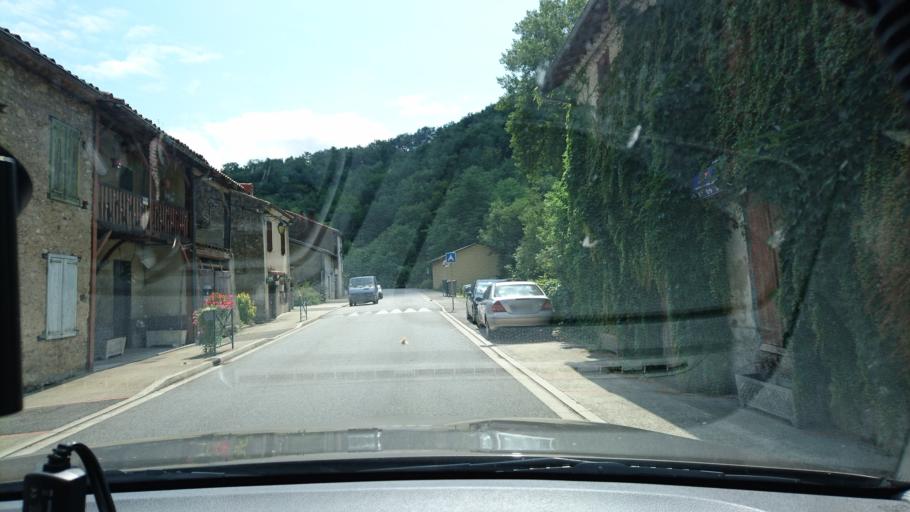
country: FR
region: Midi-Pyrenees
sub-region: Departement de la Haute-Garonne
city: Gaillac-Toulza
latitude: 43.1010
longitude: 1.4428
